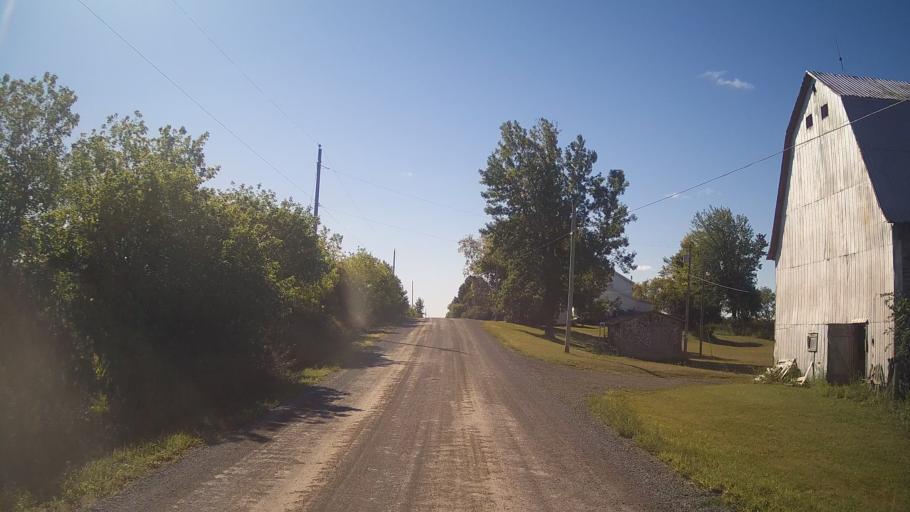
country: CA
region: Ontario
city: Prescott
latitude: 44.9767
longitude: -75.5731
